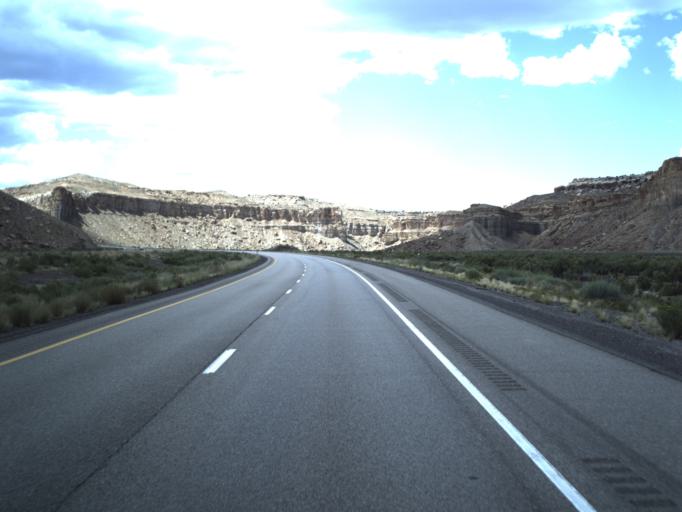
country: US
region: Utah
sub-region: Emery County
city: Ferron
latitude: 38.8103
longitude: -111.2461
